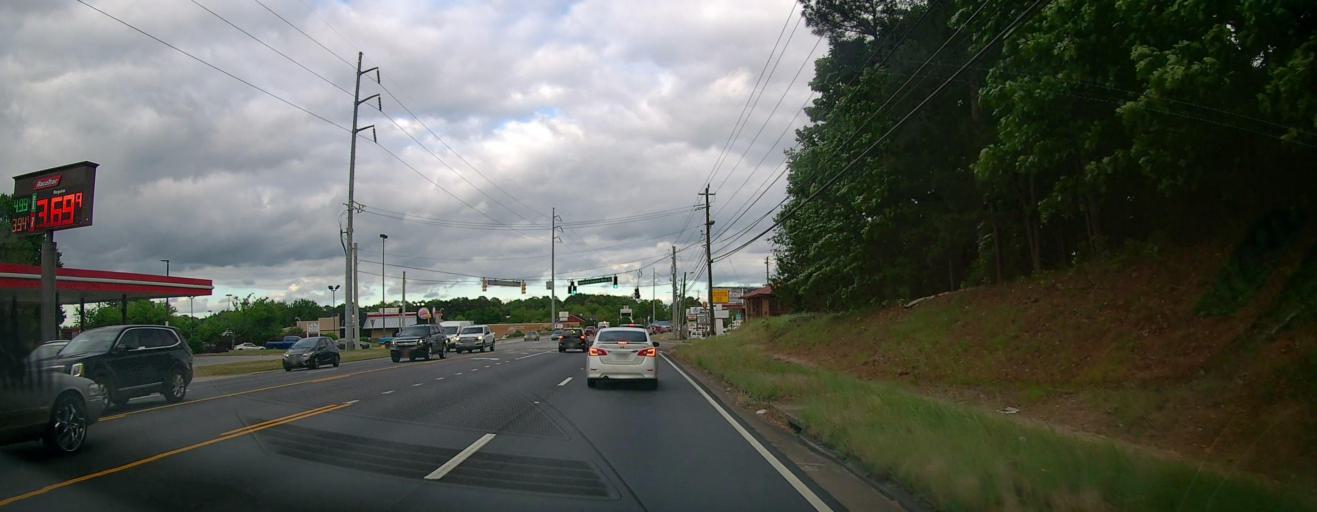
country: US
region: Georgia
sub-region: Oconee County
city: Bogart
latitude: 33.9407
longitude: -83.4709
